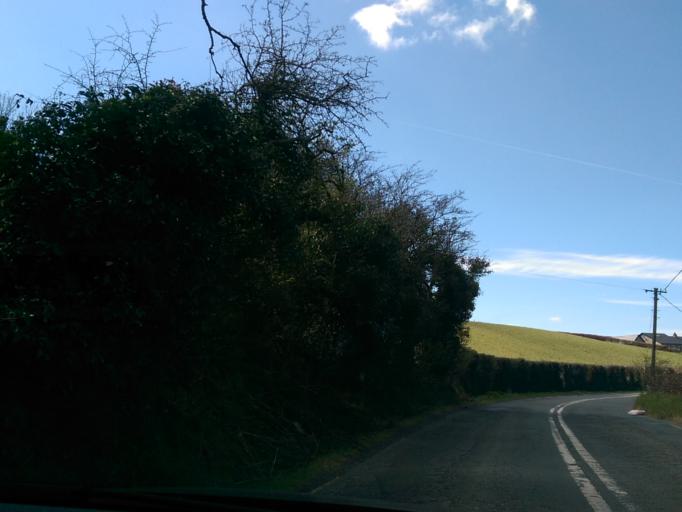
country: IE
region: Leinster
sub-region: Wicklow
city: Carnew
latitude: 52.8147
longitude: -6.4910
